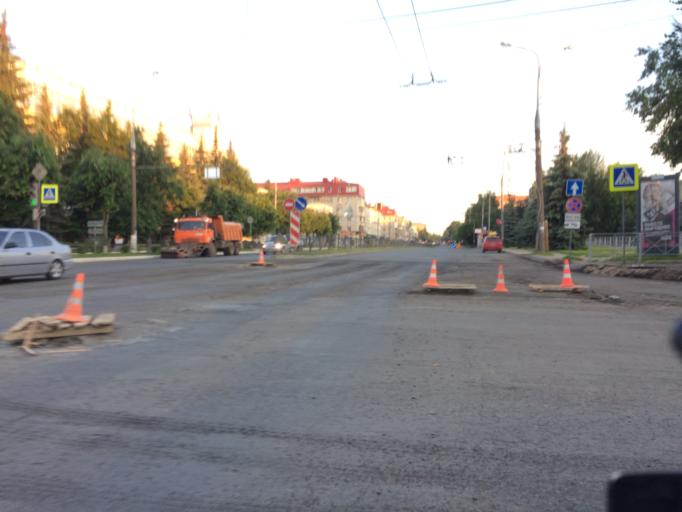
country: RU
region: Mariy-El
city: Yoshkar-Ola
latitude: 56.6405
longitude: 47.8963
